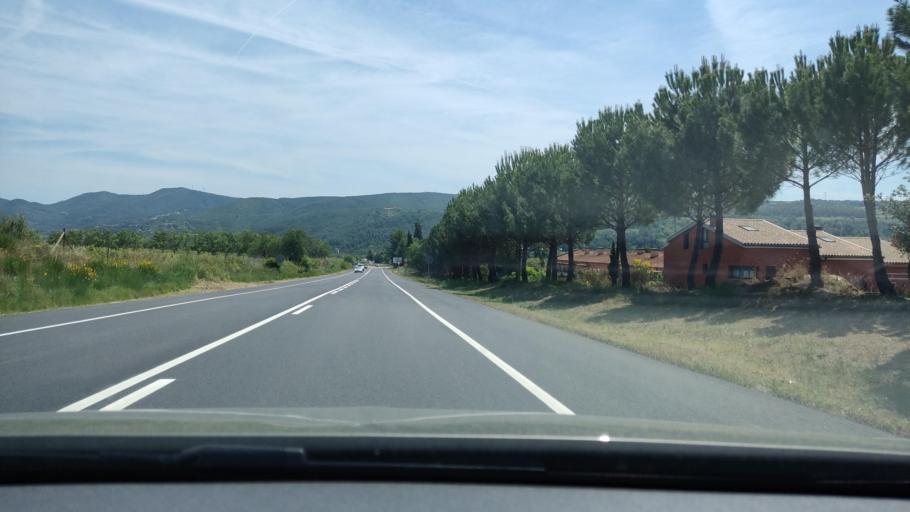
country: ES
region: Catalonia
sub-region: Provincia de Barcelona
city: Sant Sadurni d'Anoia
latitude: 41.4309
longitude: 1.7889
